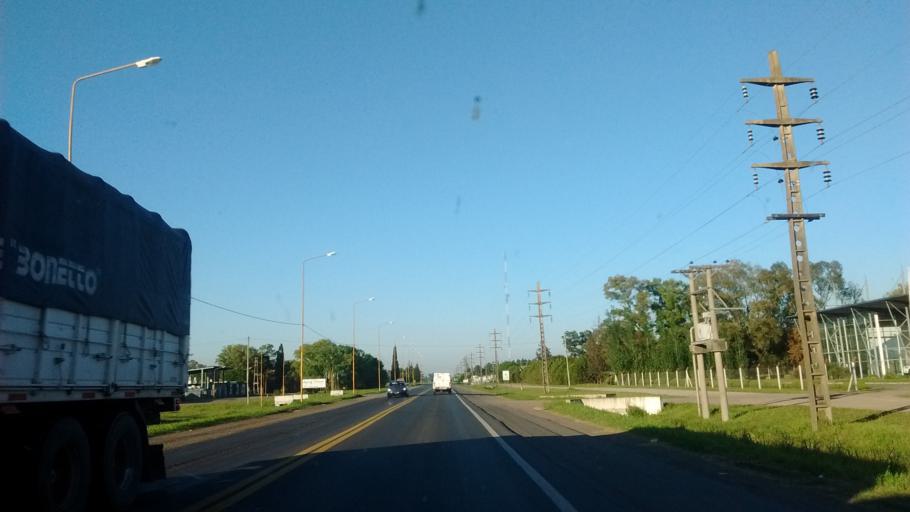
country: AR
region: Santa Fe
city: Firmat
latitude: -33.4540
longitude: -61.4988
